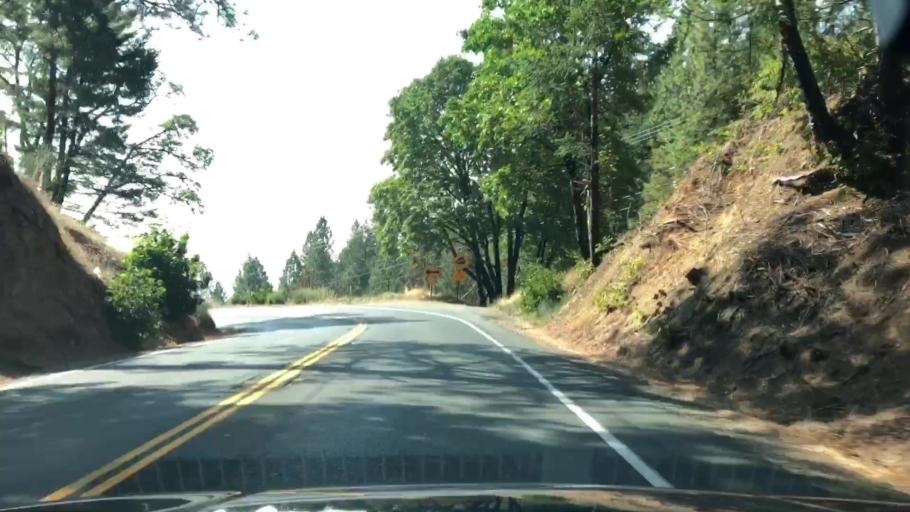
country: US
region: California
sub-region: Napa County
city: Calistoga
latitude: 38.6516
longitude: -122.5999
